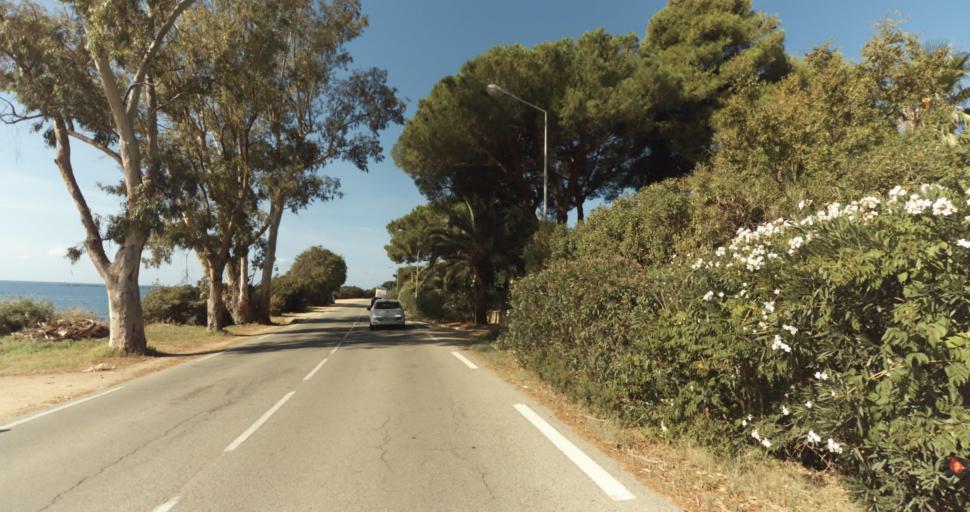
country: FR
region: Corsica
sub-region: Departement de la Corse-du-Sud
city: Ajaccio
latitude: 41.9106
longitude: 8.6419
